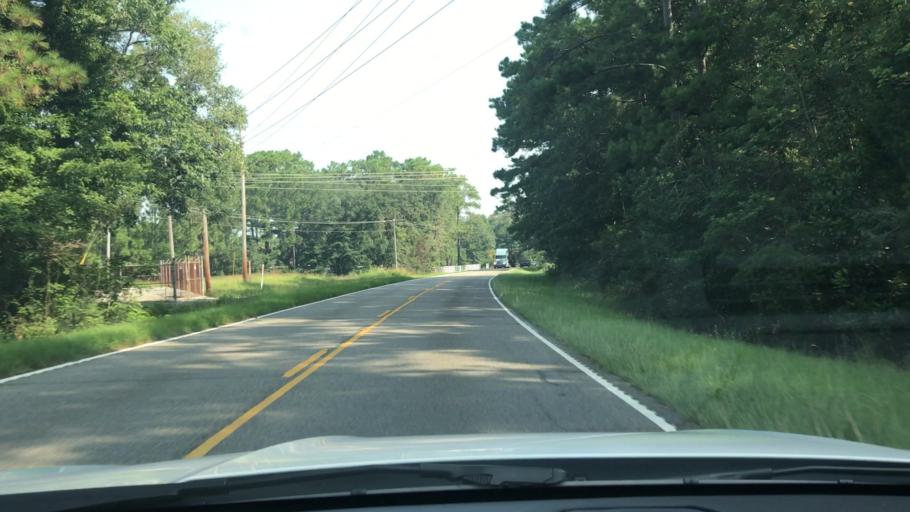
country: US
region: South Carolina
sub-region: Georgetown County
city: Georgetown
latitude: 33.4577
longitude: -79.2811
